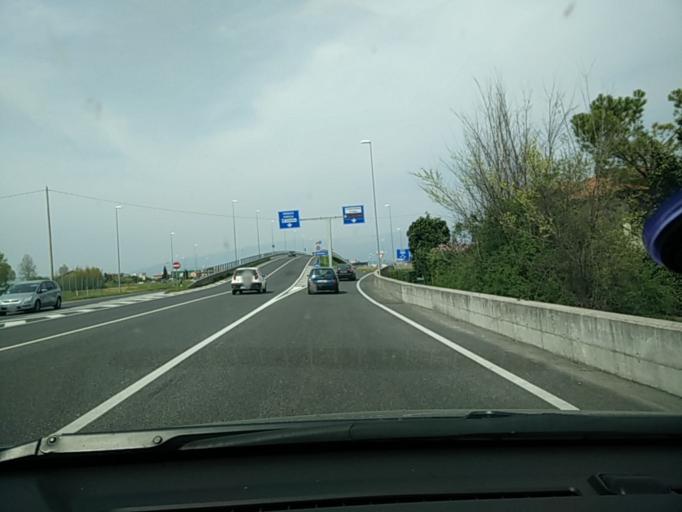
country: IT
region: Friuli Venezia Giulia
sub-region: Provincia di Pordenone
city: Cordenons
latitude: 45.9468
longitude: 12.6971
